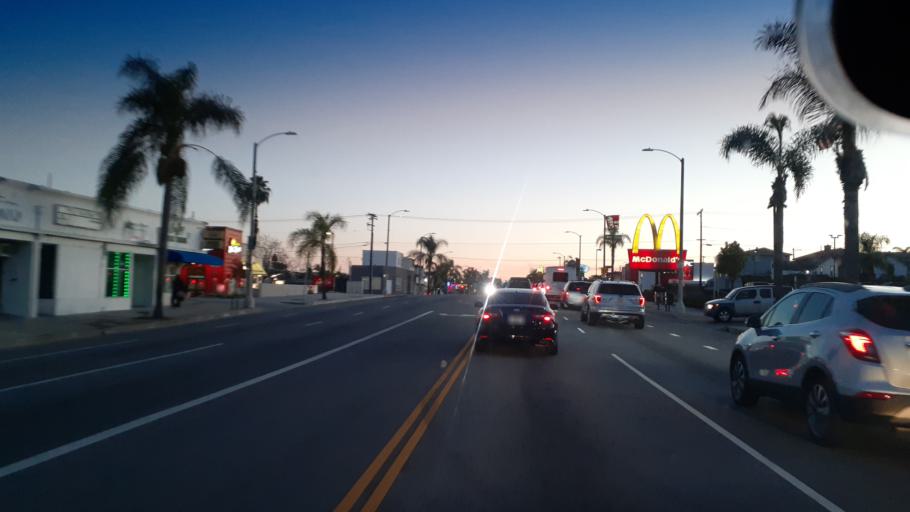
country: US
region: California
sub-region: Los Angeles County
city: San Pedro
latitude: 33.7415
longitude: -118.2924
